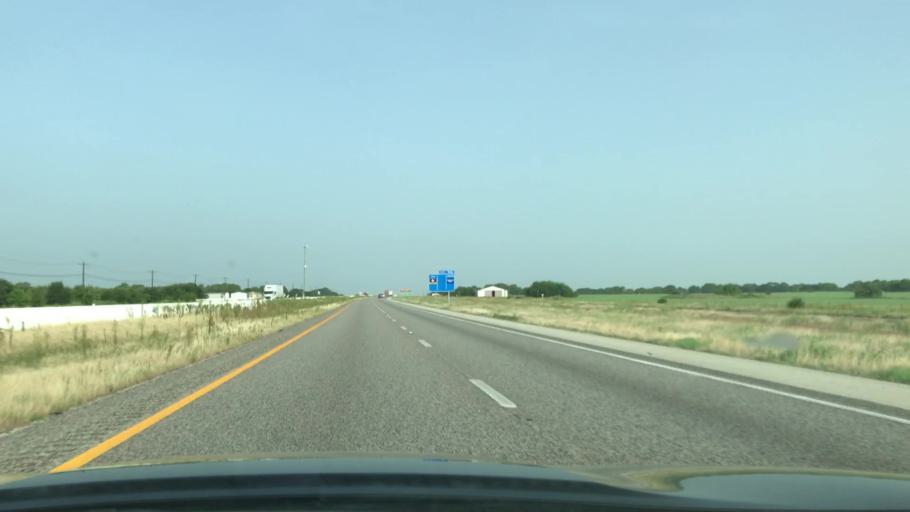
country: US
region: Texas
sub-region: Van Zandt County
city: Wills Point
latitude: 32.6268
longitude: -96.0054
